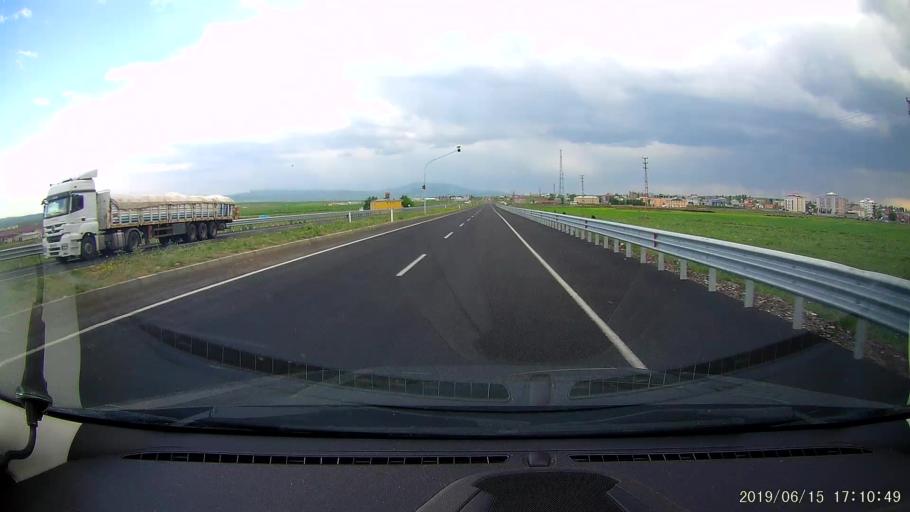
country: TR
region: Kars
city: Kars
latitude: 40.6181
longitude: 43.1334
